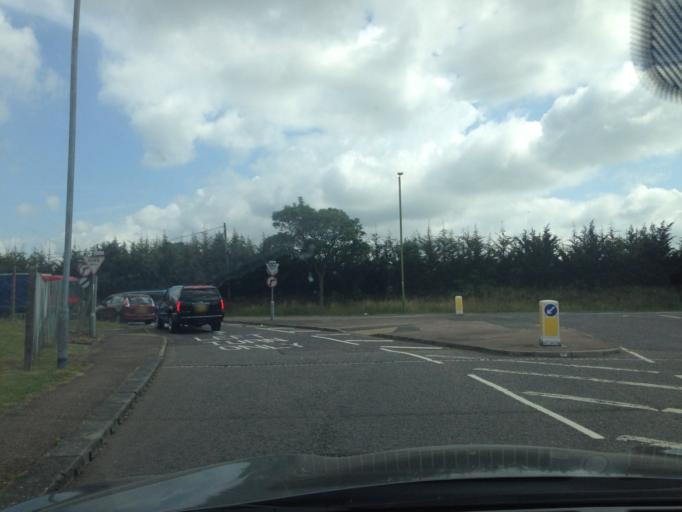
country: GB
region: England
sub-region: Hertfordshire
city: Bushey
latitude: 51.6632
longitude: -0.3594
